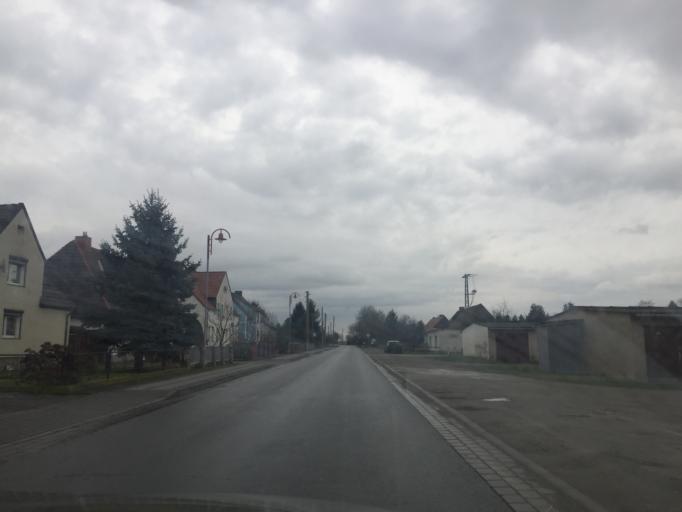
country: DE
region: Saxony-Anhalt
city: Egeln
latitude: 51.9371
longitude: 11.4316
